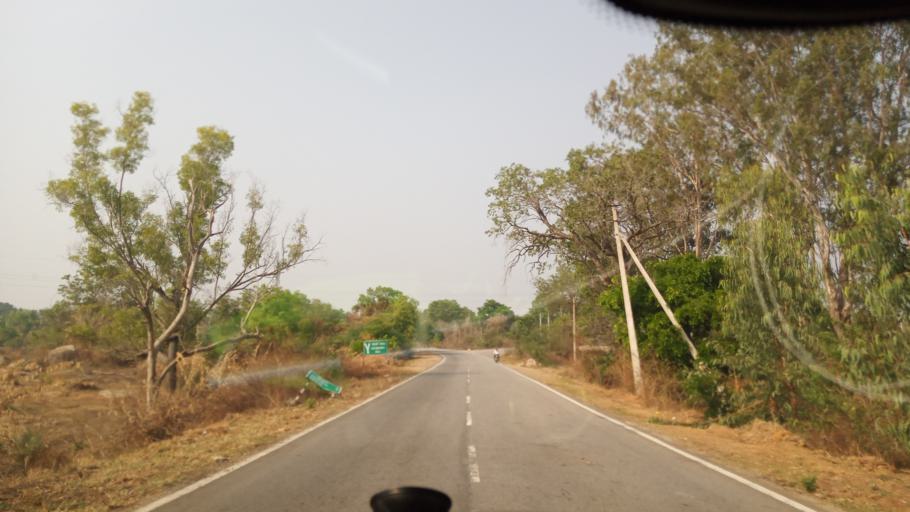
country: IN
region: Karnataka
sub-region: Mandya
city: Belluru
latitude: 12.9497
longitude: 76.7523
